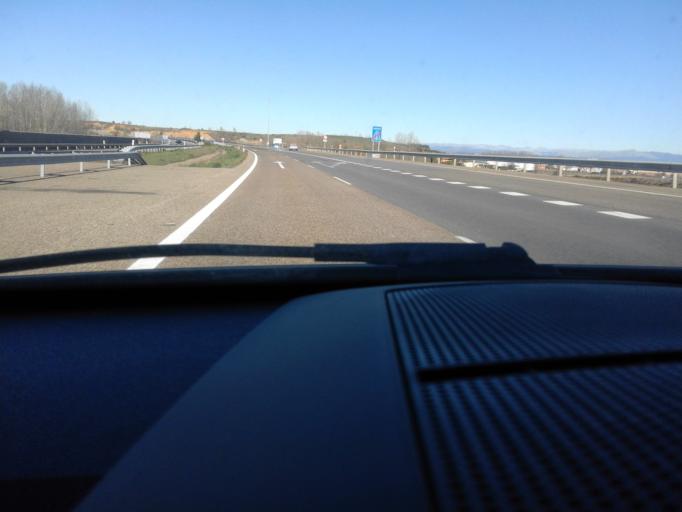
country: ES
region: Castille and Leon
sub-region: Provincia de Leon
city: Onzonilla
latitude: 42.5257
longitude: -5.5945
